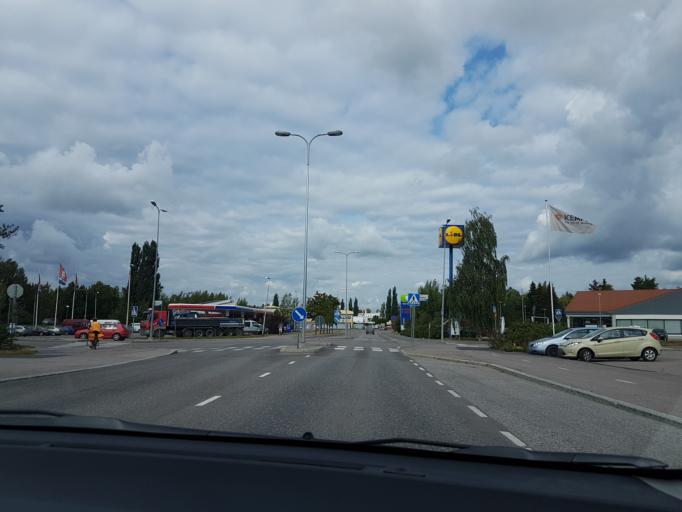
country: FI
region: Uusimaa
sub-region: Helsinki
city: Jaervenpaeae
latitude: 60.4741
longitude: 25.1124
